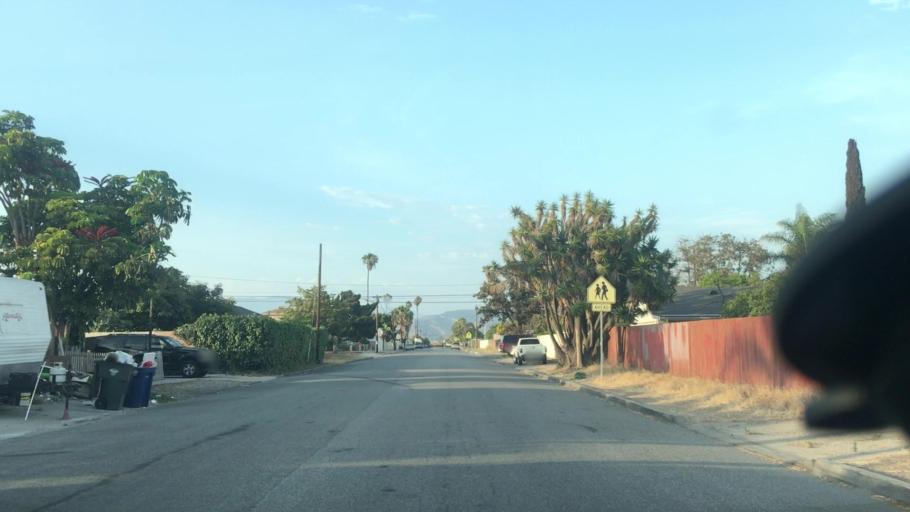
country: US
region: California
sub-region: Ventura County
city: El Rio
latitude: 34.2380
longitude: -119.1616
